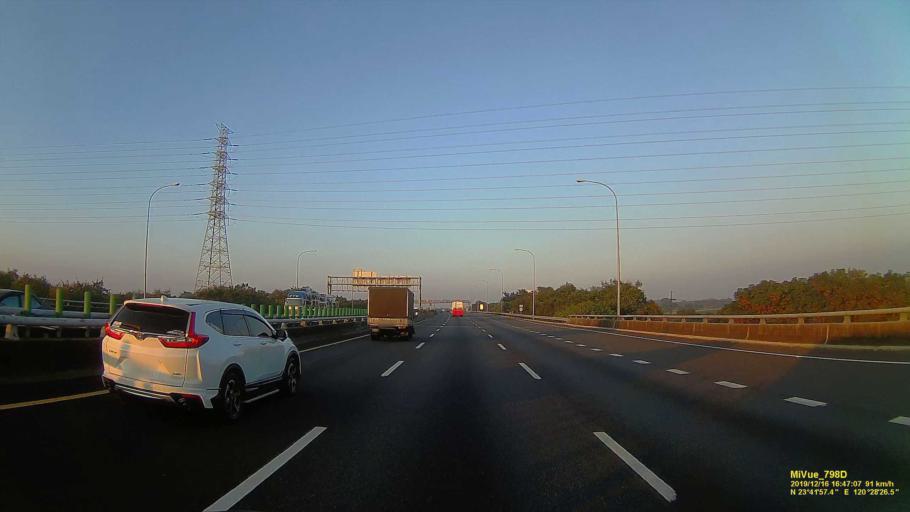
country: TW
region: Taiwan
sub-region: Yunlin
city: Douliu
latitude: 23.6997
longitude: 120.4741
